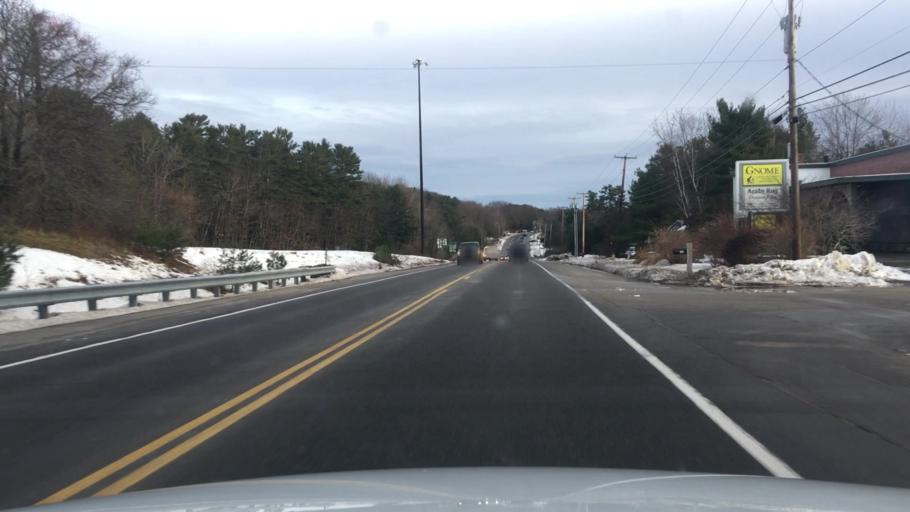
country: US
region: Maine
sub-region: Cumberland County
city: Falmouth
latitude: 43.7305
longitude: -70.2287
